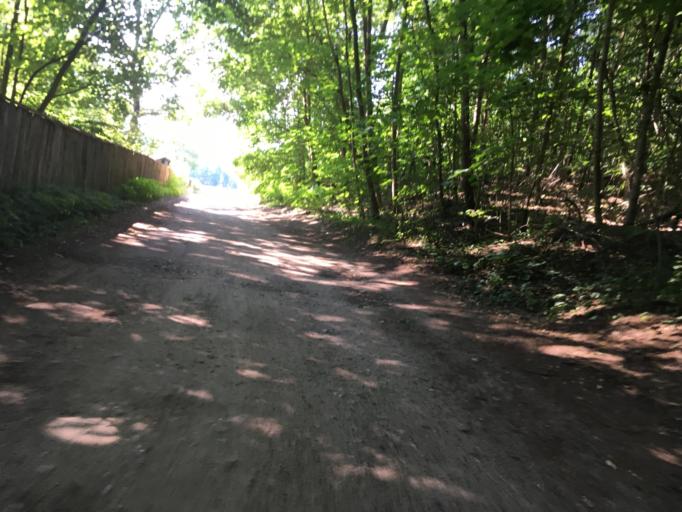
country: DE
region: Brandenburg
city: Templin
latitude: 53.1301
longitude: 13.5498
